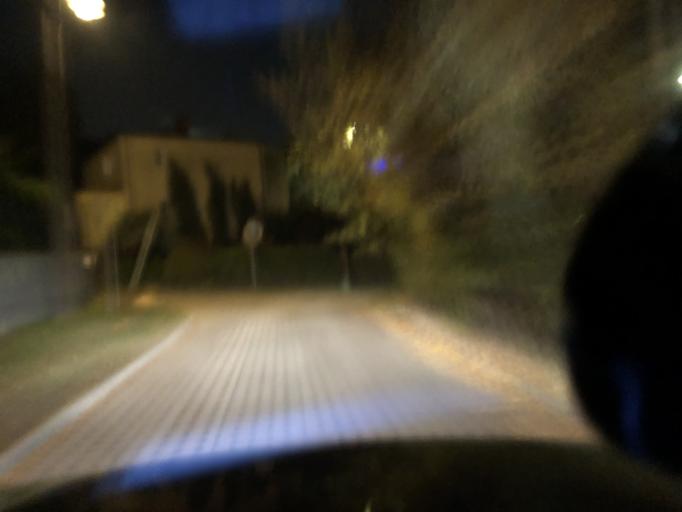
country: PL
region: Pomeranian Voivodeship
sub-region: Powiat gdanski
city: Kowale
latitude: 54.3424
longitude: 18.5773
